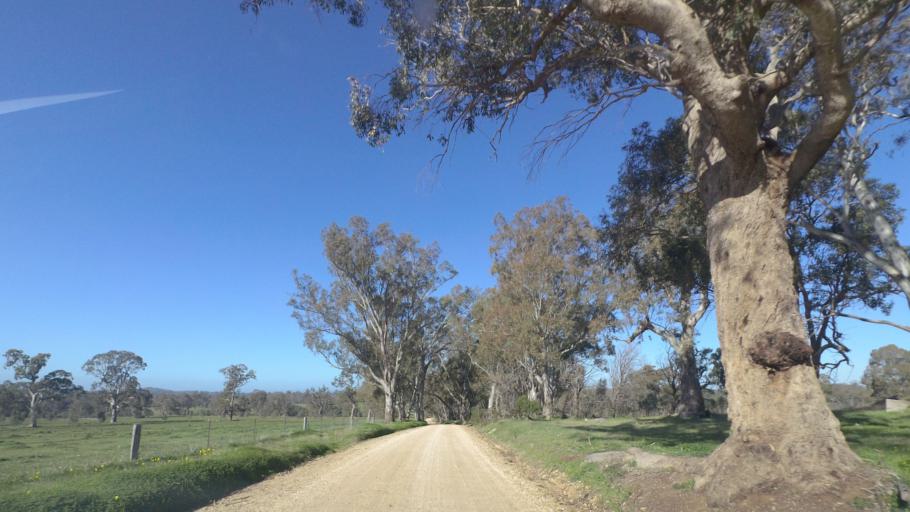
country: AU
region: Victoria
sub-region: Mount Alexander
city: Castlemaine
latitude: -36.9645
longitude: 144.3425
